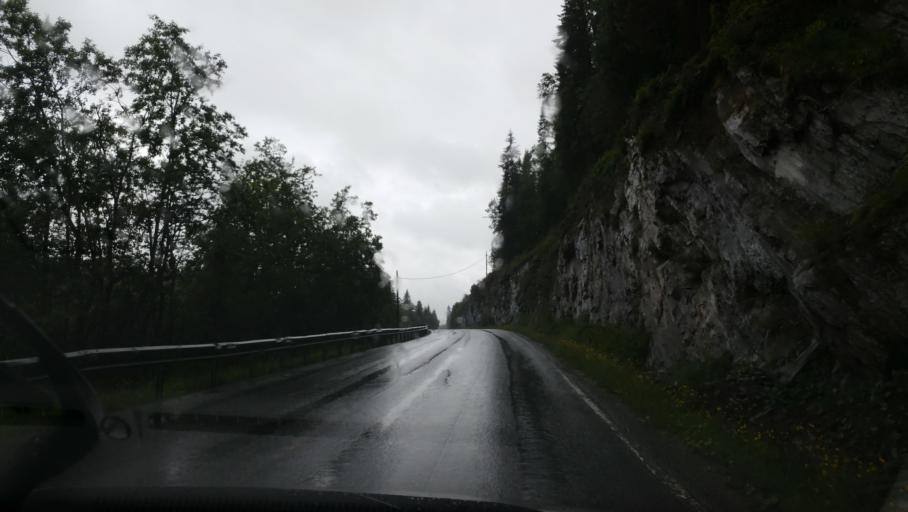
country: NO
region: Sor-Trondelag
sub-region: Selbu
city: Mebonden
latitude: 63.3116
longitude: 11.0807
